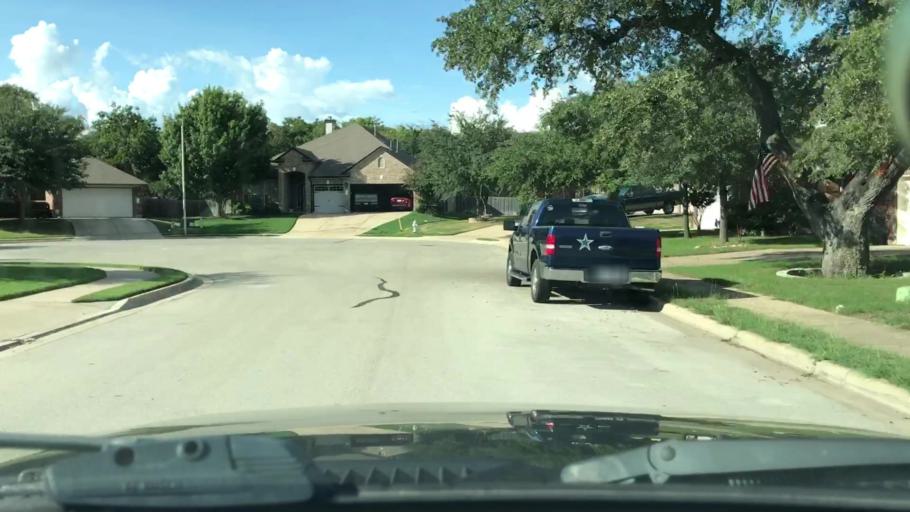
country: US
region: Texas
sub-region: Williamson County
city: Leander
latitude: 30.5429
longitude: -97.8548
